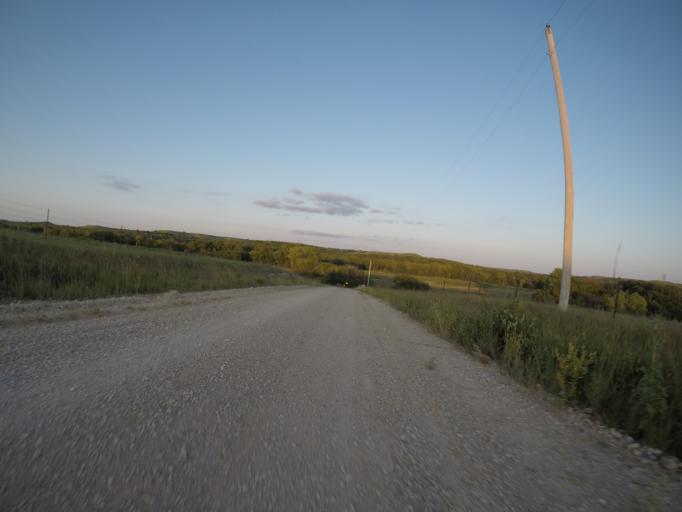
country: US
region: Kansas
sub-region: Riley County
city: Ogden
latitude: 39.0069
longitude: -96.6040
